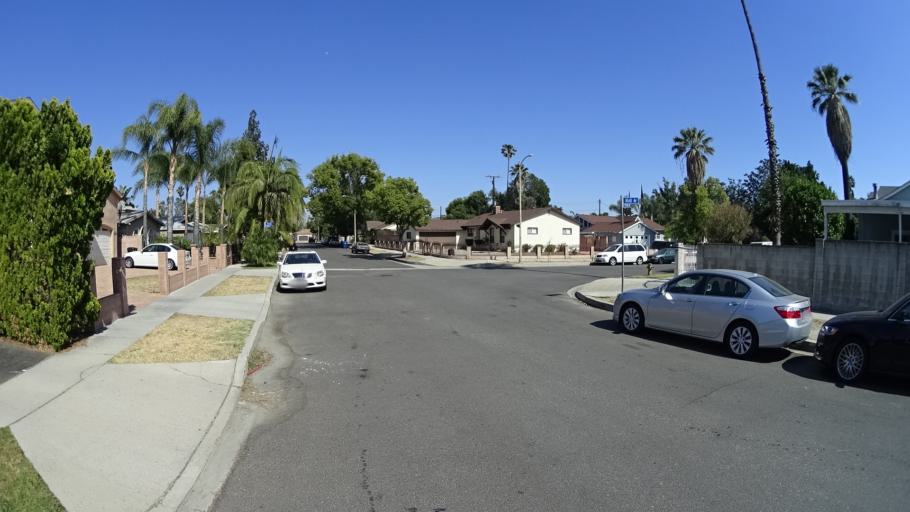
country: US
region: California
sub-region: Los Angeles County
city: Van Nuys
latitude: 34.2150
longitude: -118.4185
